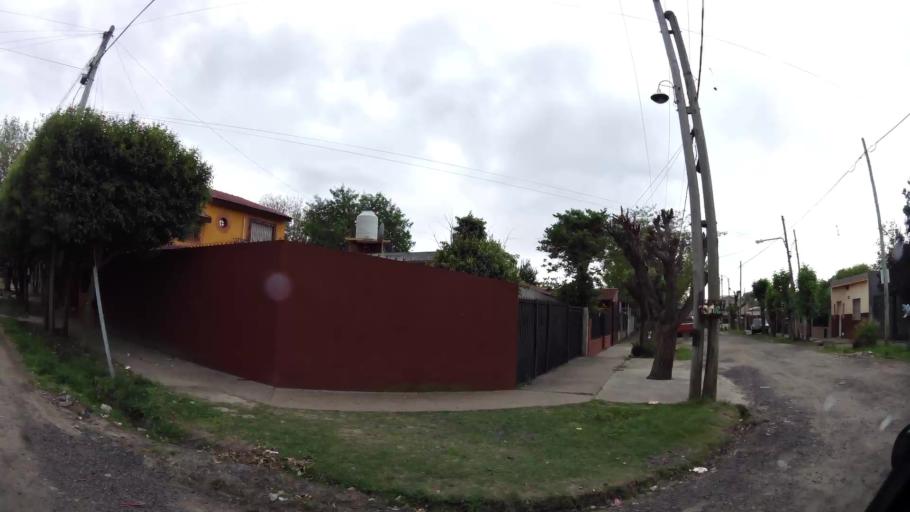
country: AR
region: Buenos Aires
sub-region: Partido de Quilmes
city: Quilmes
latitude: -34.7924
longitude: -58.2646
